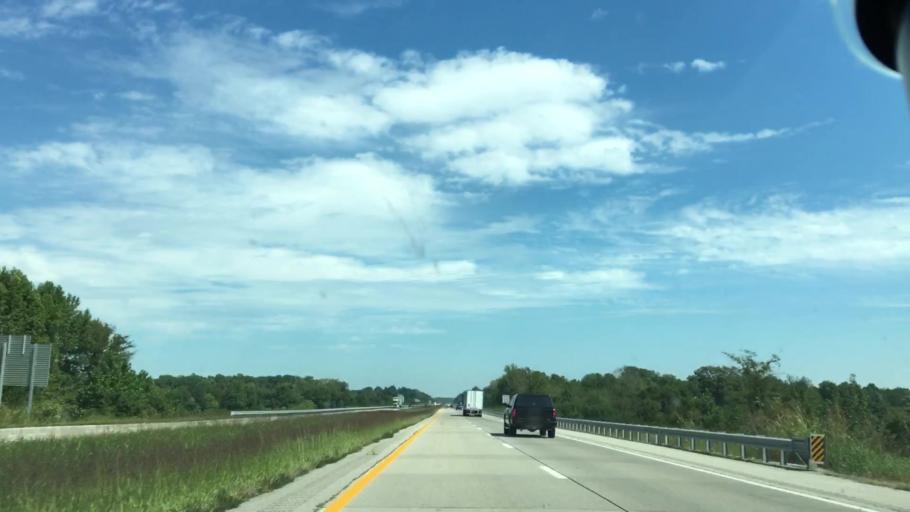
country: US
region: Kentucky
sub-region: Daviess County
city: Owensboro
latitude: 37.7575
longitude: -87.2555
